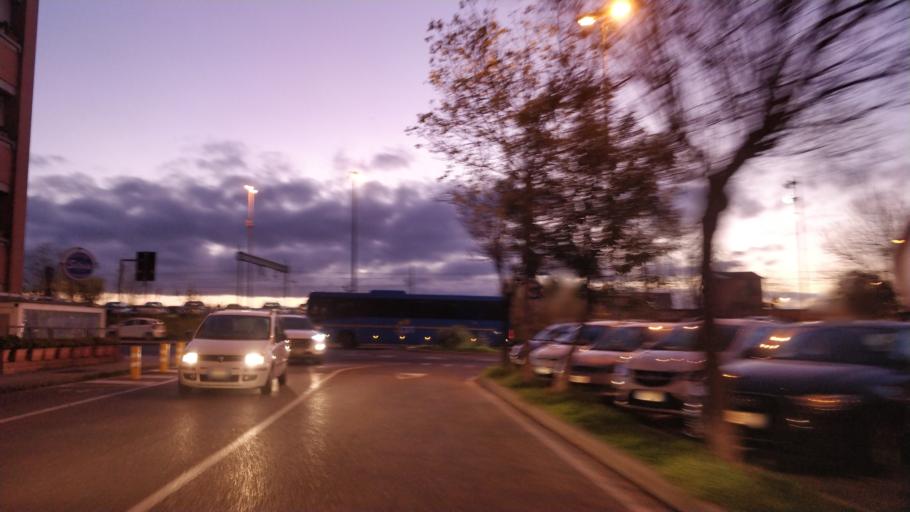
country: IT
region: Tuscany
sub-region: Provincia di Livorno
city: Cecina
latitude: 43.3138
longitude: 10.5135
